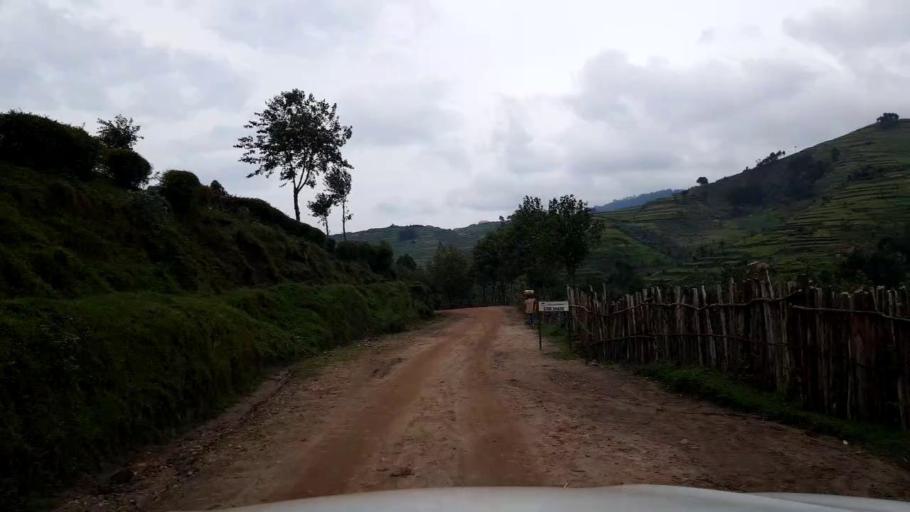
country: RW
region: Western Province
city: Kibuye
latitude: -1.9552
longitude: 29.4227
